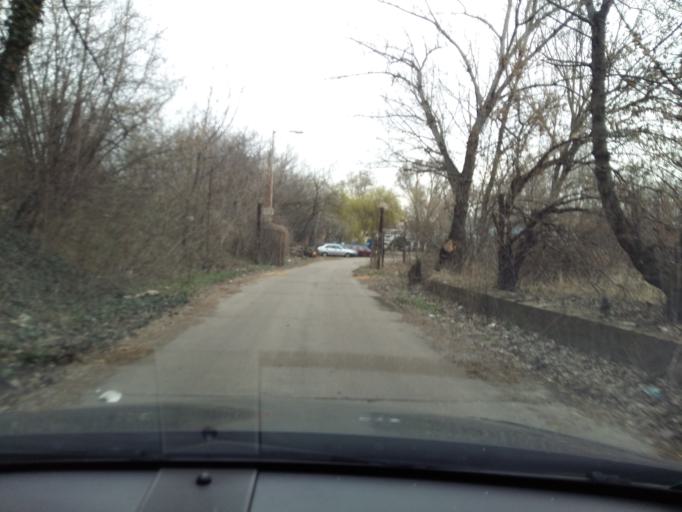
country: HU
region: Budapest
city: Budapest XIII. keruelet
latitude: 47.5364
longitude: 19.0943
